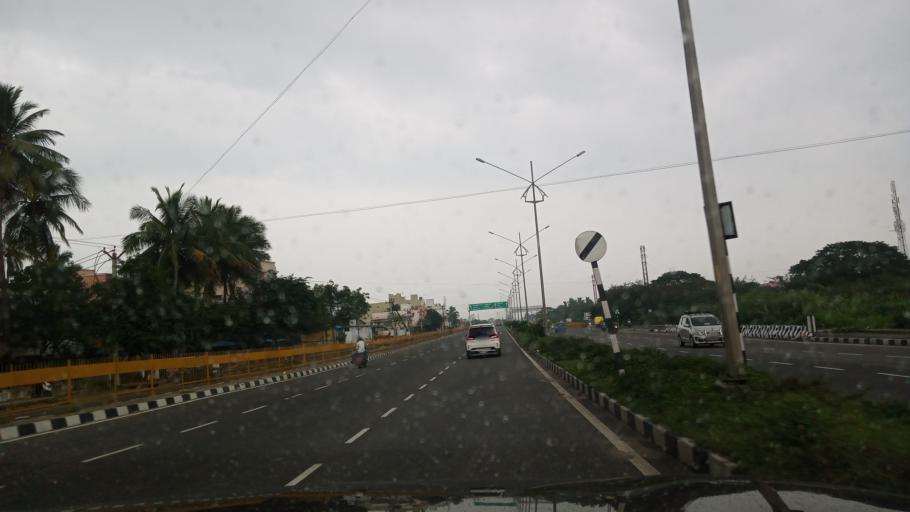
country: IN
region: Tamil Nadu
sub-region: Vellore
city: Arcot
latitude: 12.9213
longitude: 79.3314
